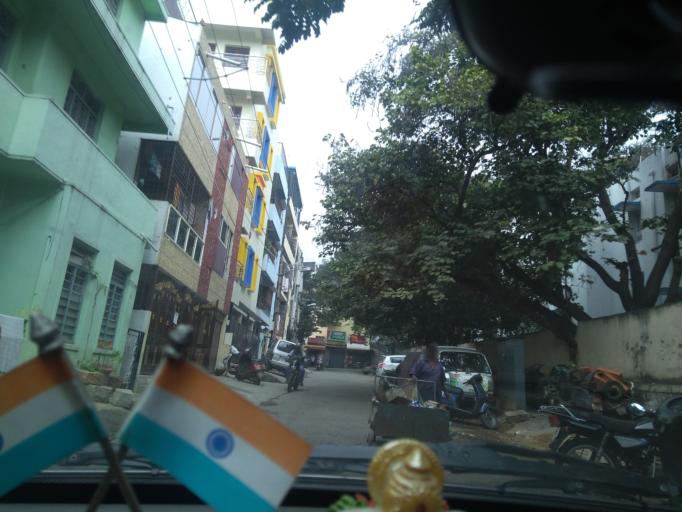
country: IN
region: Karnataka
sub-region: Bangalore Urban
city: Bangalore
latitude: 12.9843
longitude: 77.5555
